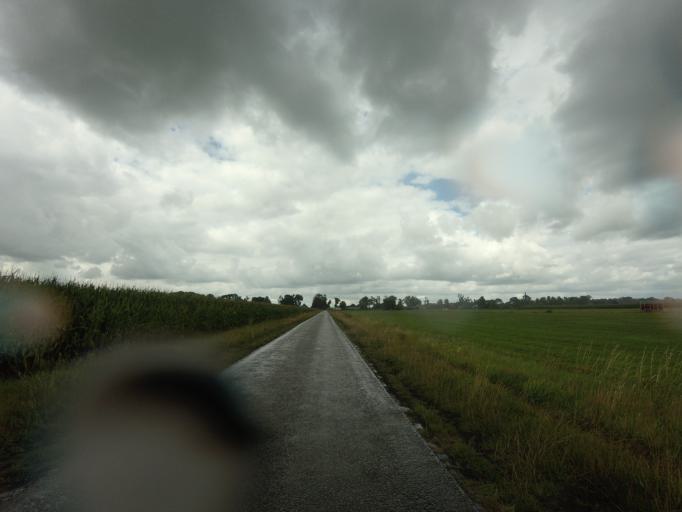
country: NL
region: Overijssel
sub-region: Gemeente Steenwijkerland
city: Wanneperveen
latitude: 52.7198
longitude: 6.1567
